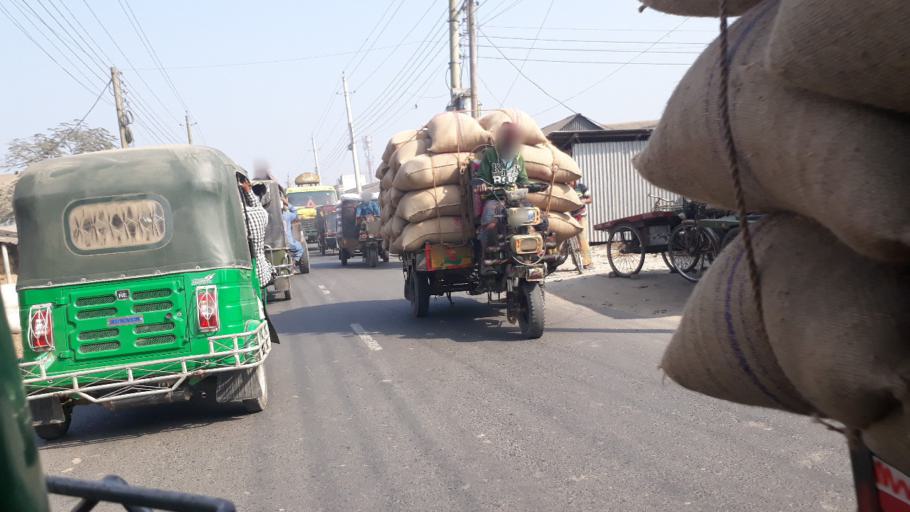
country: BD
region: Khulna
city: Kushtia
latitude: 23.8691
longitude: 89.0662
